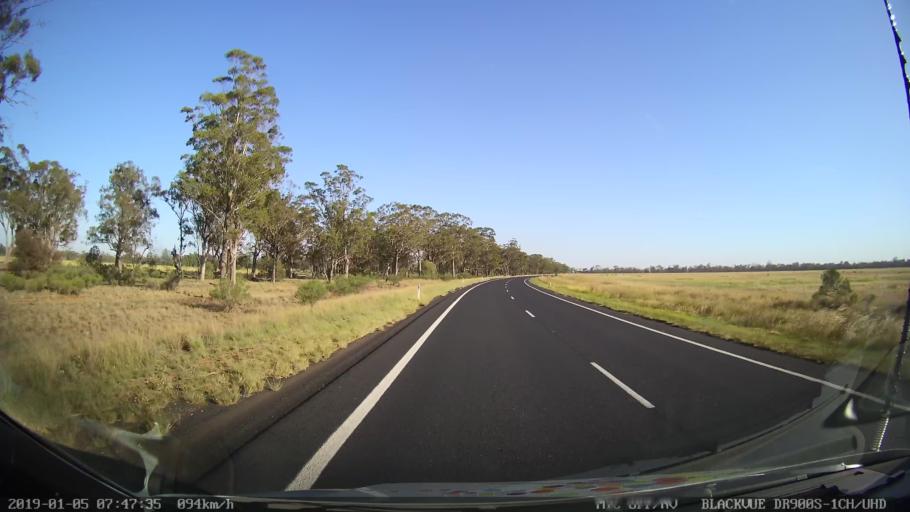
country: AU
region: New South Wales
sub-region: Gilgandra
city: Gilgandra
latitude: -31.8285
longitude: 148.6384
